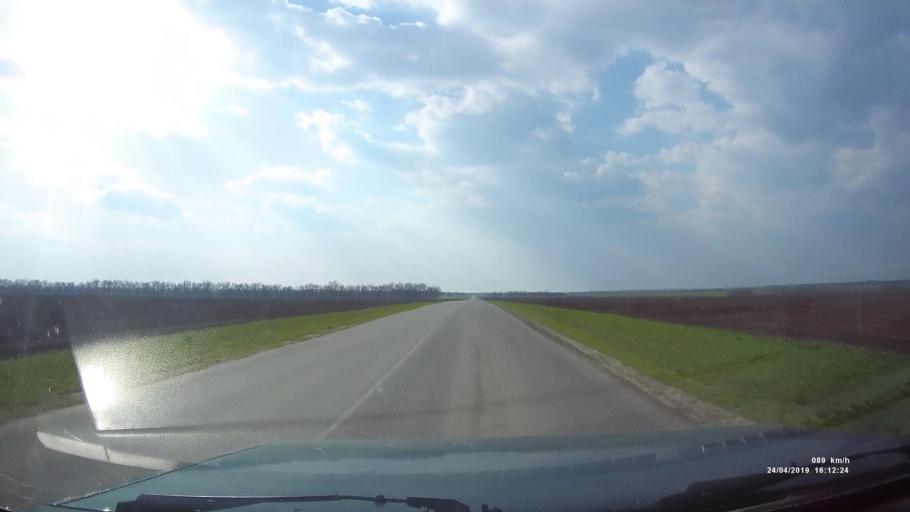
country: RU
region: Rostov
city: Sovetskoye
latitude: 46.7326
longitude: 42.2380
